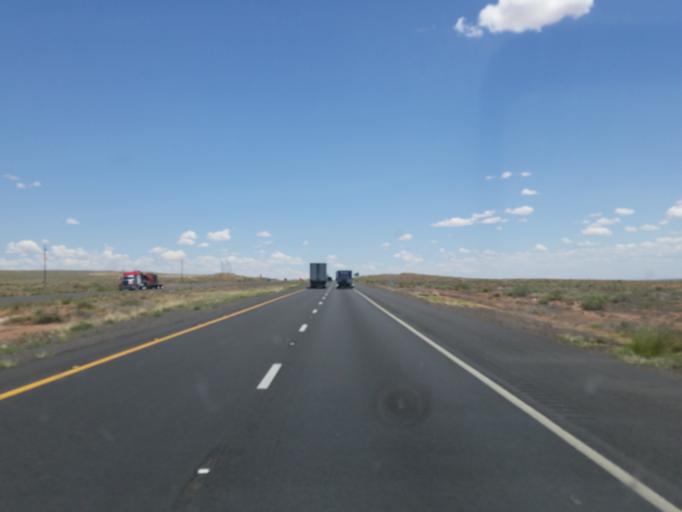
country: US
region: Arizona
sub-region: Navajo County
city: Winslow
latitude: 34.9794
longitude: -110.5384
